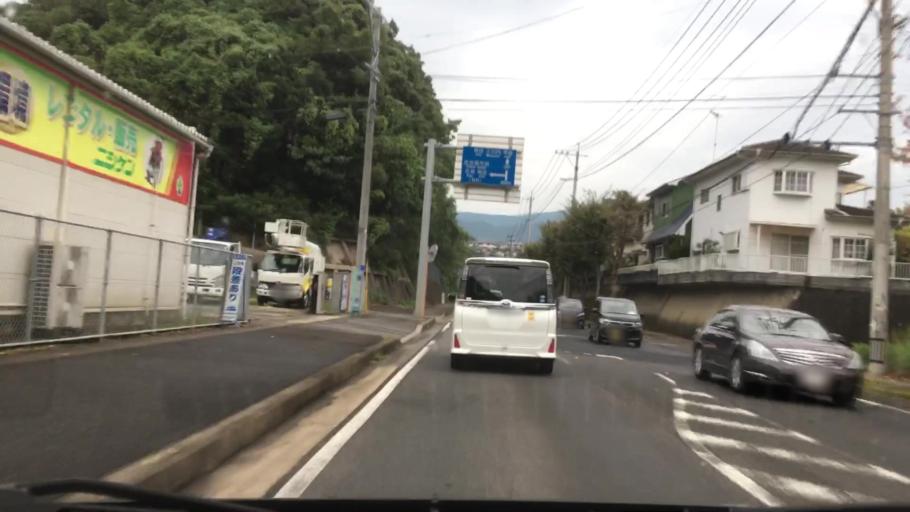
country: JP
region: Nagasaki
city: Sasebo
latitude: 33.1278
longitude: 129.7923
